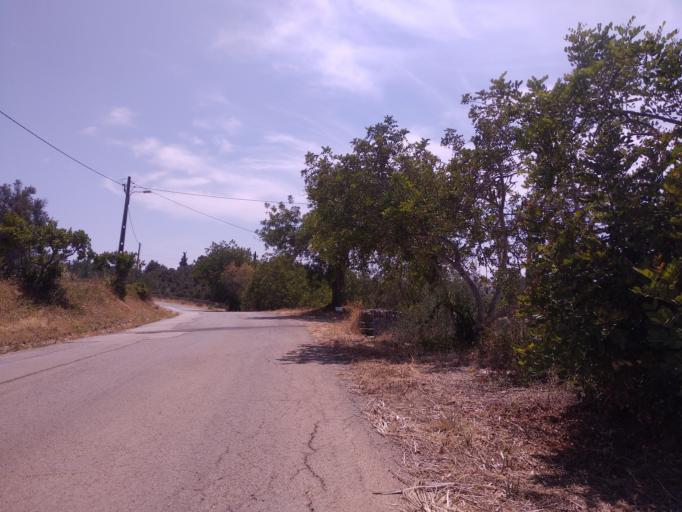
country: PT
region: Faro
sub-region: Faro
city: Santa Barbara de Nexe
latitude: 37.1245
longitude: -7.9386
